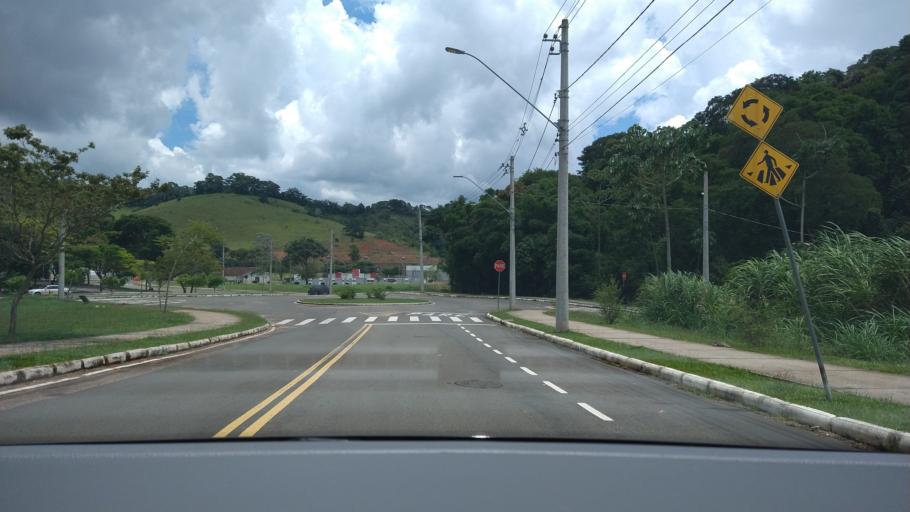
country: BR
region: Minas Gerais
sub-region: Vicosa
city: Vicosa
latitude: -20.7657
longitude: -42.8597
